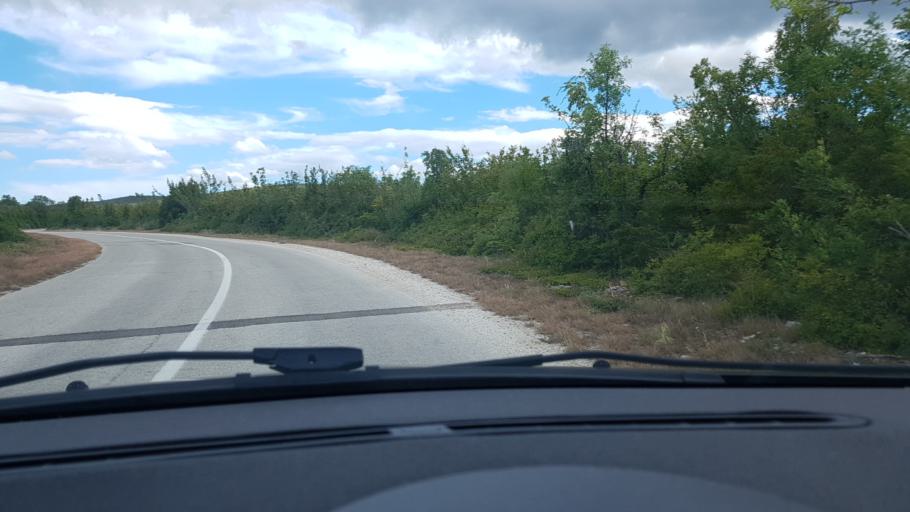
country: HR
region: Sibensko-Kniniska
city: Kistanje
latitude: 44.0941
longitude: 15.9362
